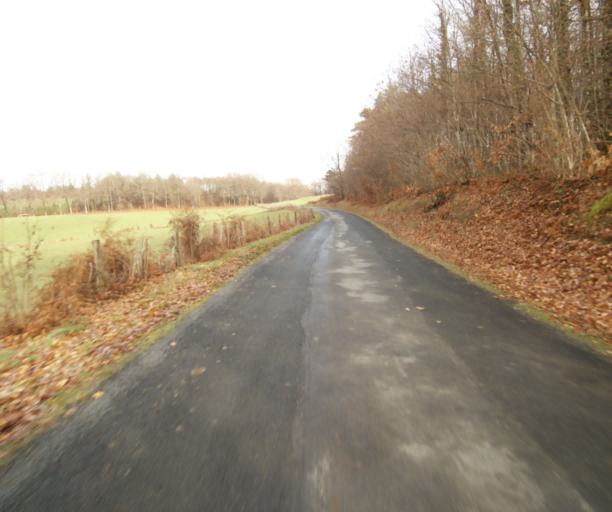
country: FR
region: Limousin
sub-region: Departement de la Correze
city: Chameyrat
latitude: 45.2493
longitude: 1.6958
